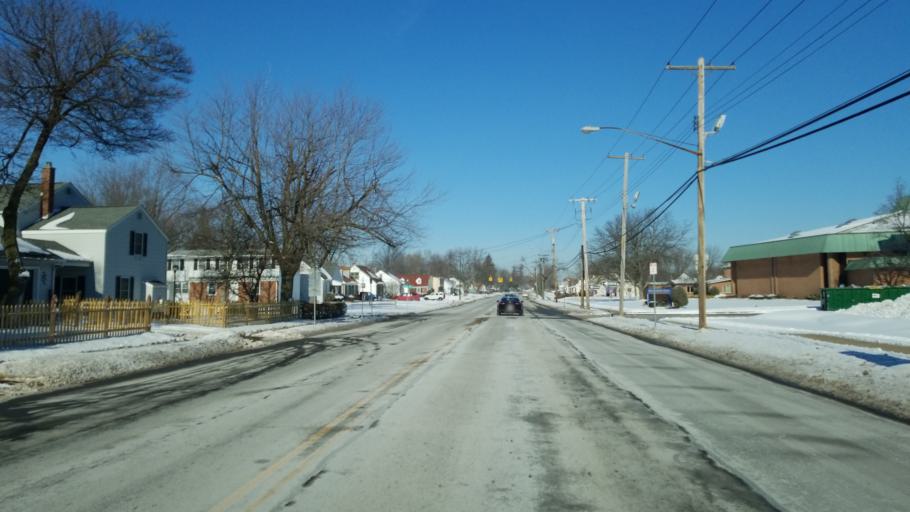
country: US
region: New York
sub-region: Erie County
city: Tonawanda
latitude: 42.9941
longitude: -78.8454
